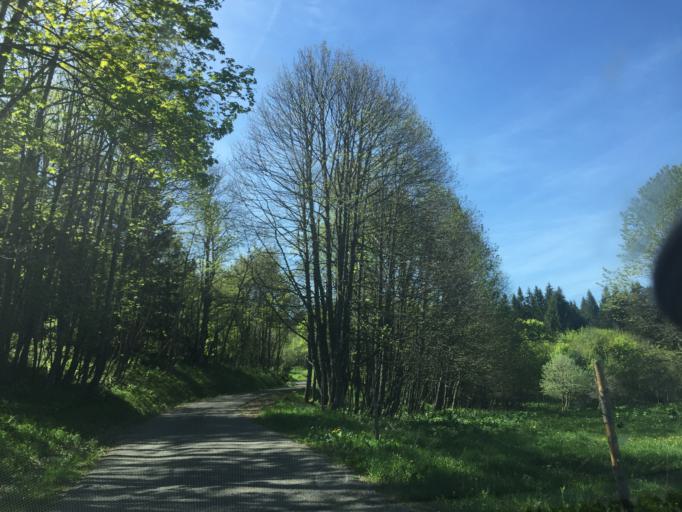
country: FR
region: Rhone-Alpes
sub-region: Departement de l'Isere
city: Saint-Ismier
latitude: 45.2968
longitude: 5.8170
